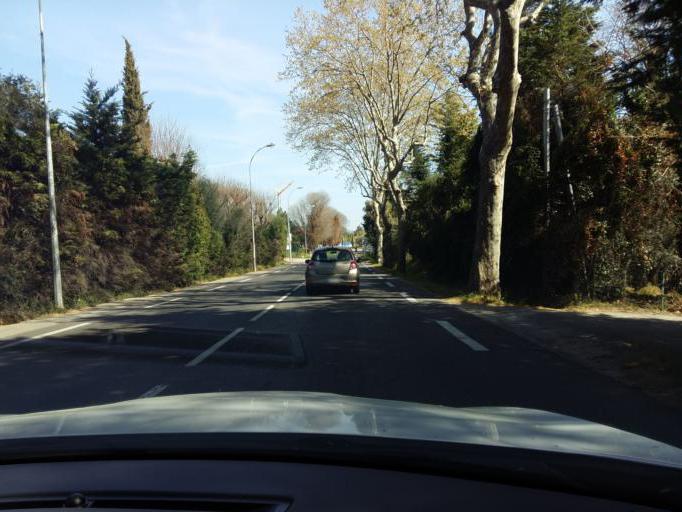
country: FR
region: Provence-Alpes-Cote d'Azur
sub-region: Departement du Var
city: Ollioules
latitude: 43.1311
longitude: 5.8719
